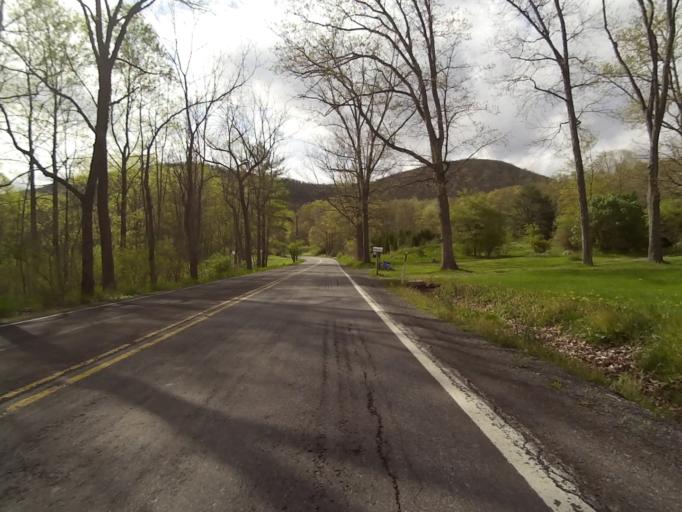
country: US
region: Pennsylvania
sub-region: Centre County
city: Park Forest Village
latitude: 40.8871
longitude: -77.9770
